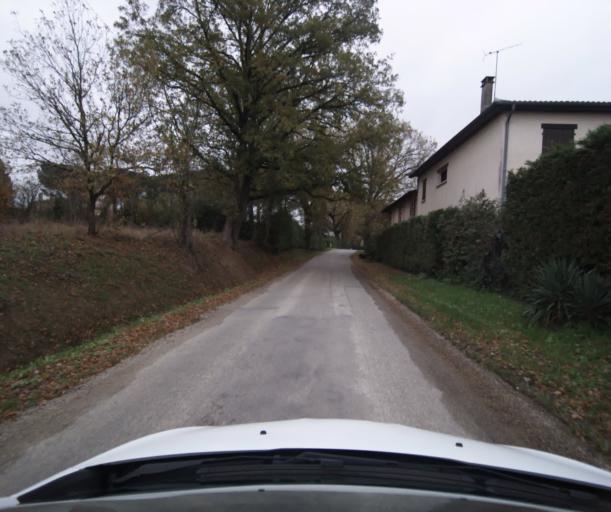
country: FR
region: Midi-Pyrenees
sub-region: Departement du Tarn-et-Garonne
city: Moissac
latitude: 44.0742
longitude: 1.1331
